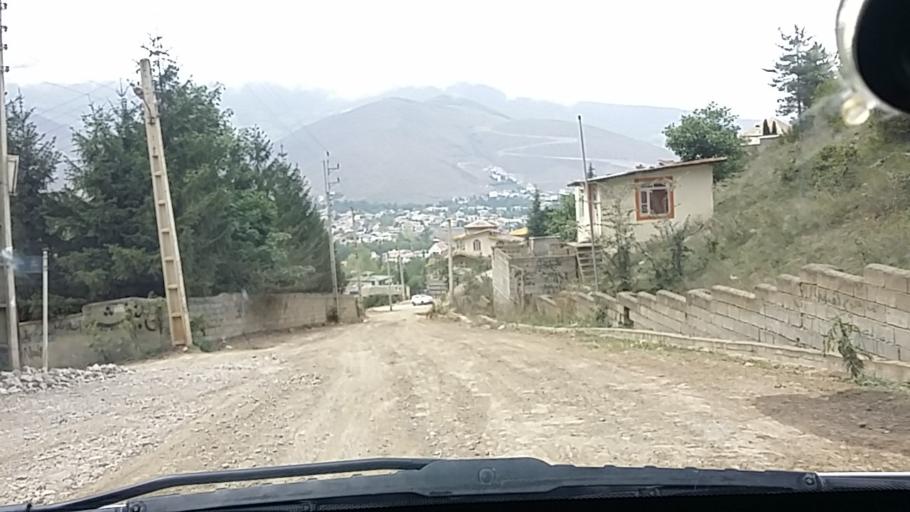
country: IR
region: Mazandaran
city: `Abbasabad
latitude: 36.4919
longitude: 51.1668
